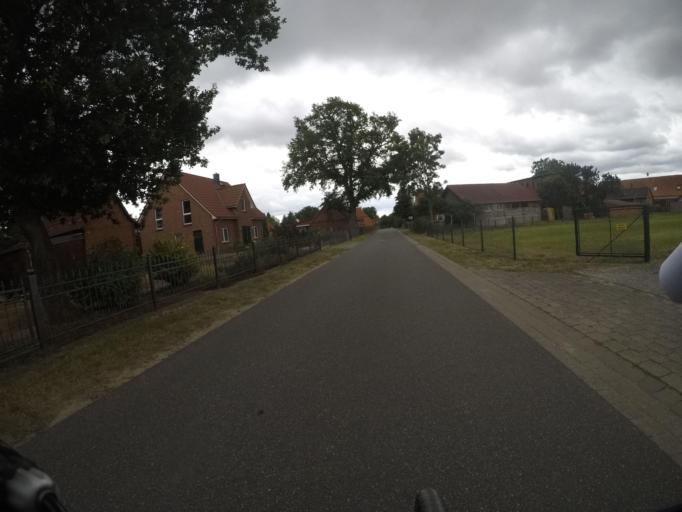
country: DE
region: Lower Saxony
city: Neu Darchau
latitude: 53.2802
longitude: 10.9350
